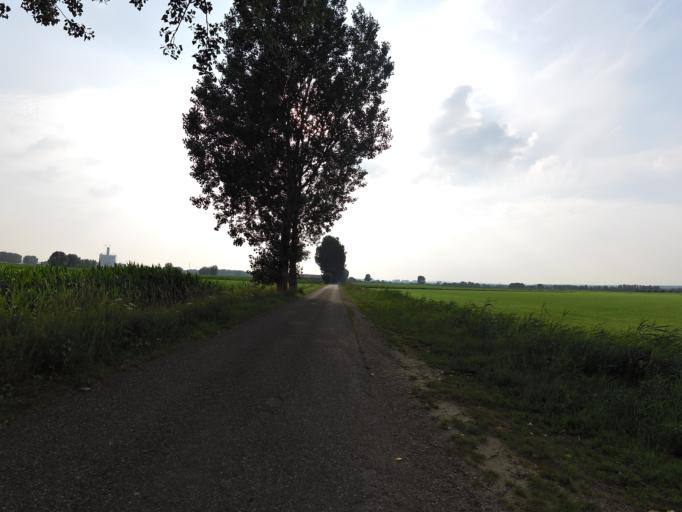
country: NL
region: Gelderland
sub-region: Gemeente Rheden
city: Rheden
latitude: 51.9783
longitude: 6.0199
